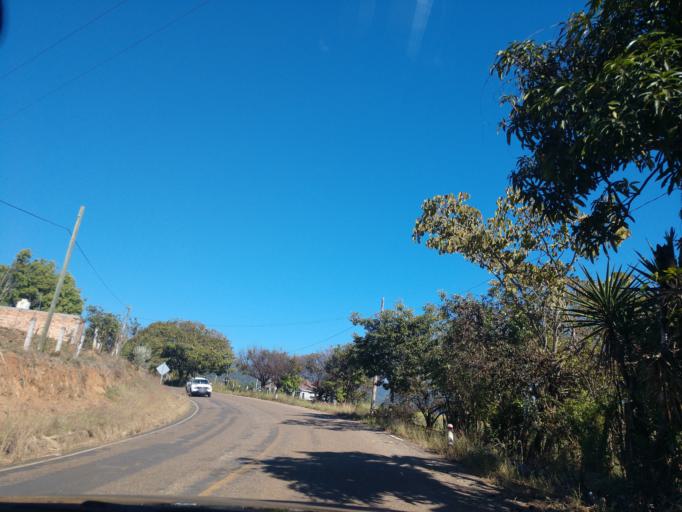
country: MX
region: Nayarit
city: Compostela
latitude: 21.2714
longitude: -104.8890
